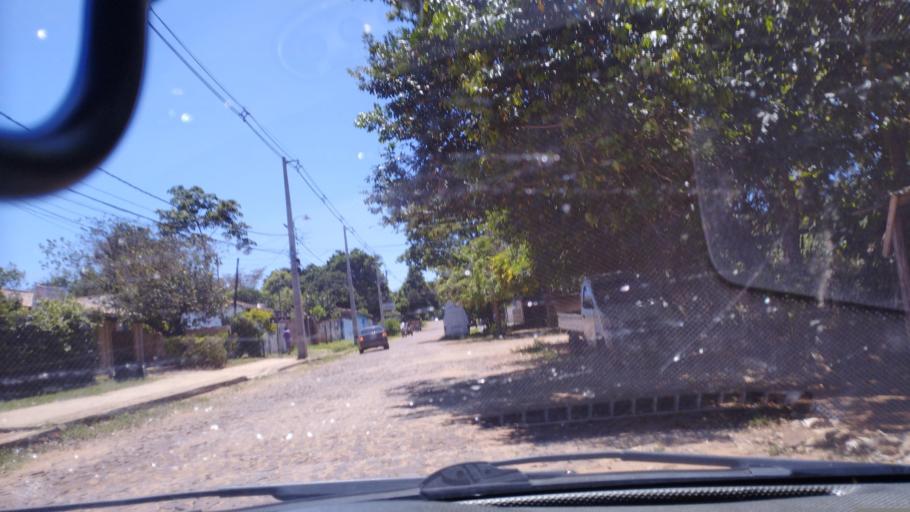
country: PY
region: Central
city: Nemby
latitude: -25.3754
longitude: -57.5413
